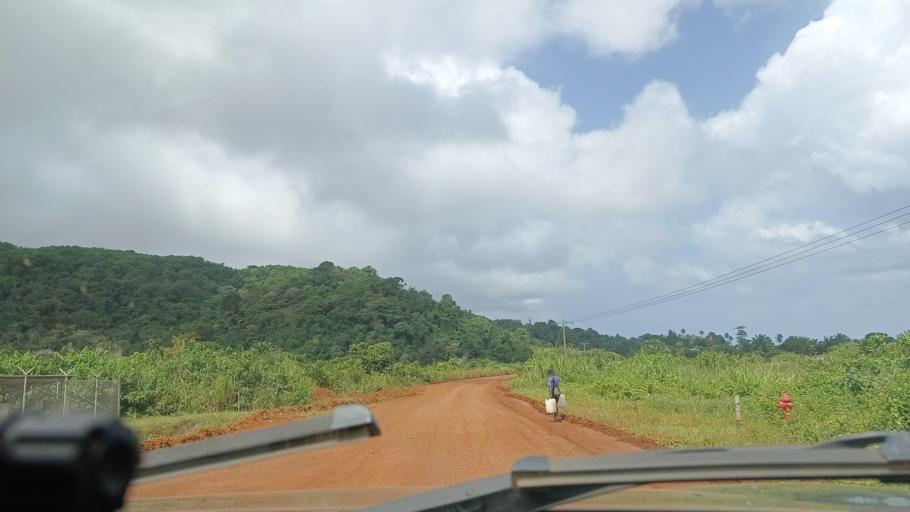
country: LR
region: Grand Cape Mount
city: Robertsport
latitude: 6.7488
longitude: -11.3579
